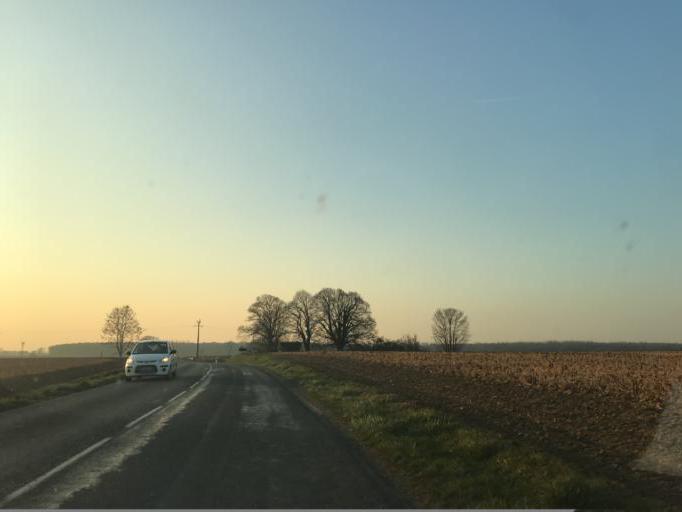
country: FR
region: Ile-de-France
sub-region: Departement de Seine-et-Marne
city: Juilly
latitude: 49.0152
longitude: 2.7384
